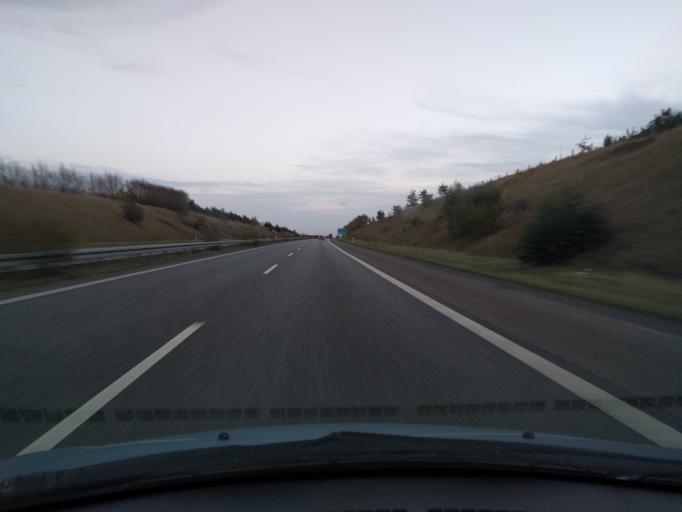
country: DK
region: South Denmark
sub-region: Faaborg-Midtfyn Kommune
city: Arslev
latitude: 55.2767
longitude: 10.4593
